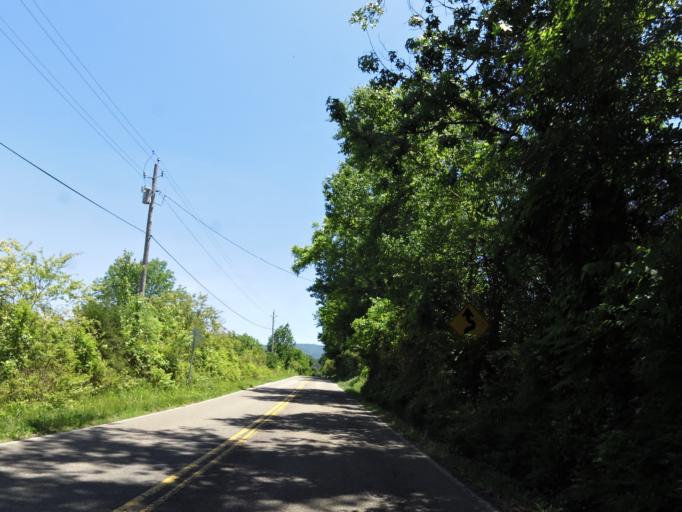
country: US
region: Tennessee
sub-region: Jefferson County
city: Dandridge
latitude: 35.9294
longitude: -83.3485
